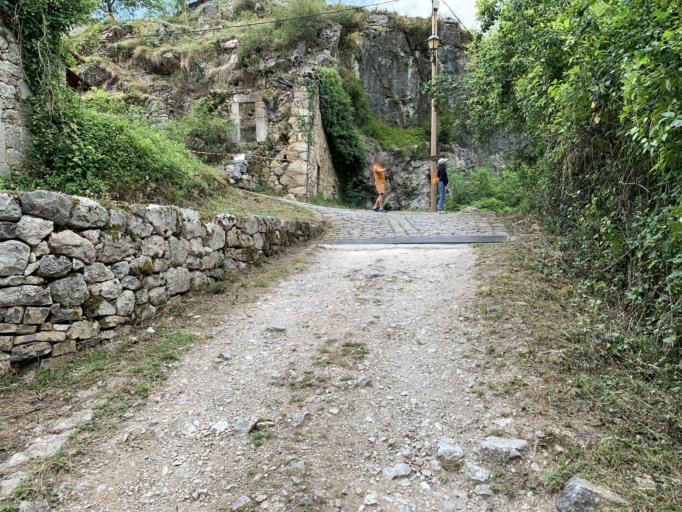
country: ES
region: Asturias
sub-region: Province of Asturias
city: Carrena
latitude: 43.2366
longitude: -4.8255
